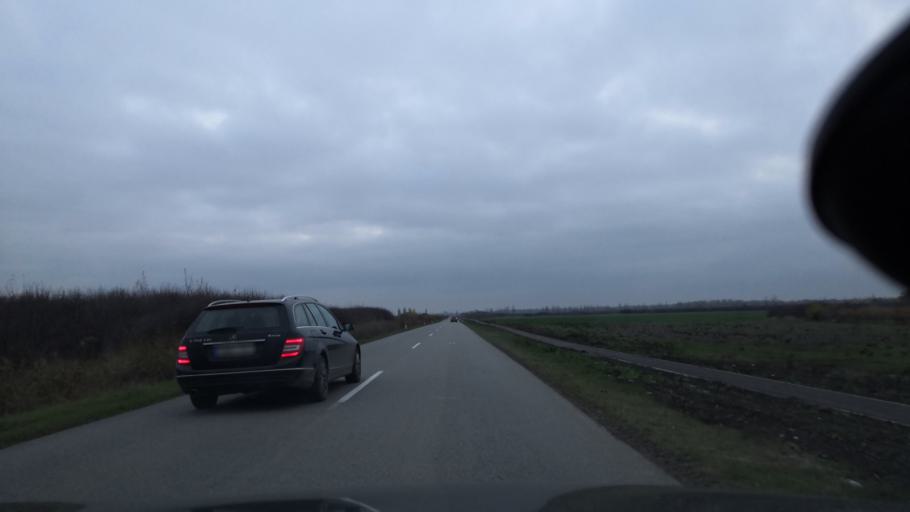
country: RS
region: Autonomna Pokrajina Vojvodina
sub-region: Severnobanatski Okrug
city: Novi Knezevac
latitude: 46.0886
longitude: 20.1089
